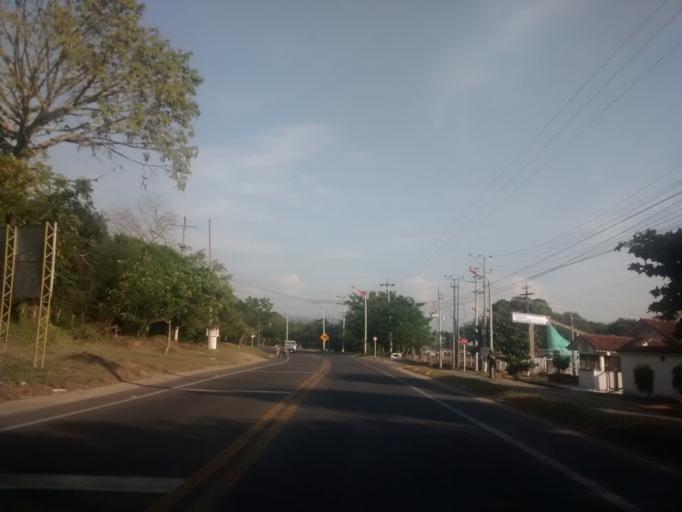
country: CO
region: Cundinamarca
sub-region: Girardot
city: Girardot City
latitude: 4.2962
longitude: -74.7897
